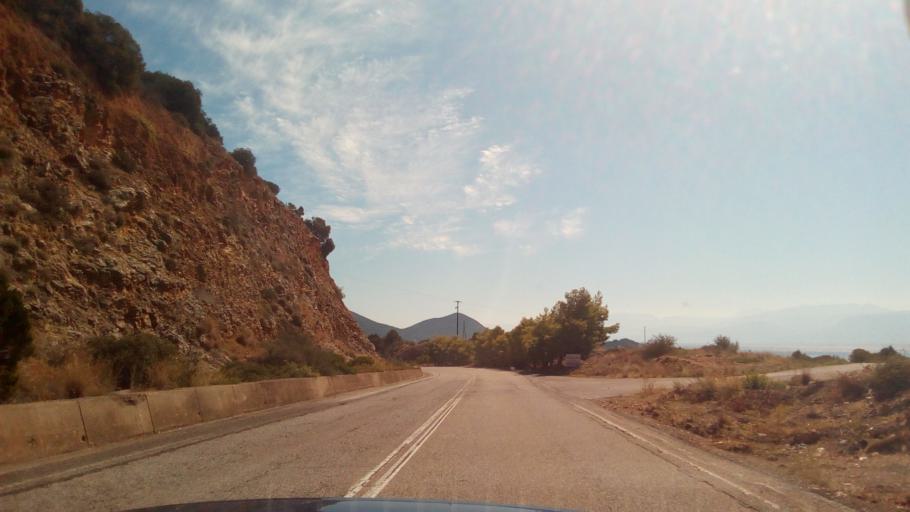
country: GR
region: West Greece
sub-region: Nomos Achaias
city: Selianitika
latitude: 38.3698
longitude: 22.1102
